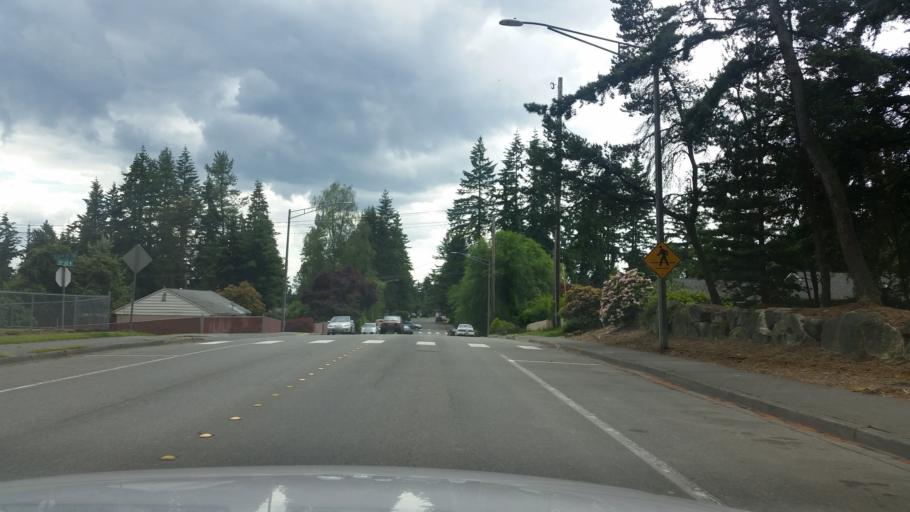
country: US
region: Washington
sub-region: Snohomish County
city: Mountlake Terrace
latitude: 47.7861
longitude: -122.3111
